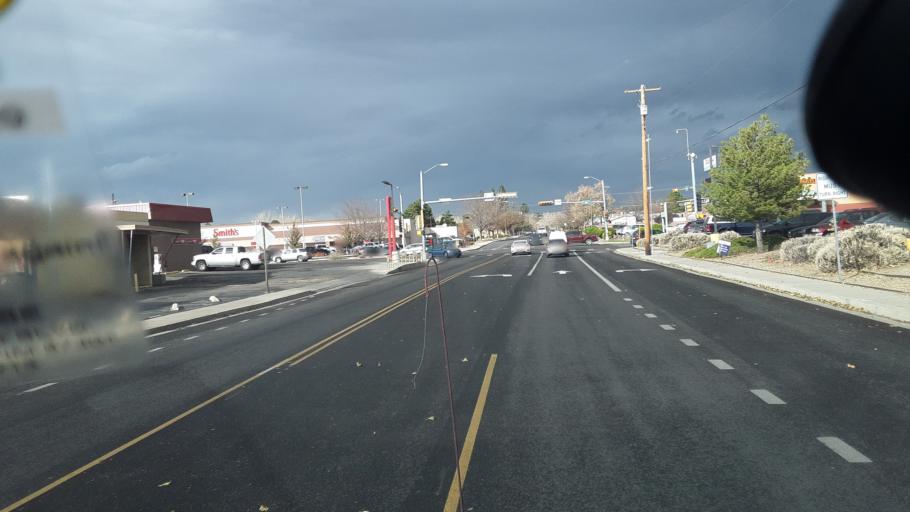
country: US
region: New Mexico
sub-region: San Juan County
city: Farmington
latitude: 36.7475
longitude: -108.1977
